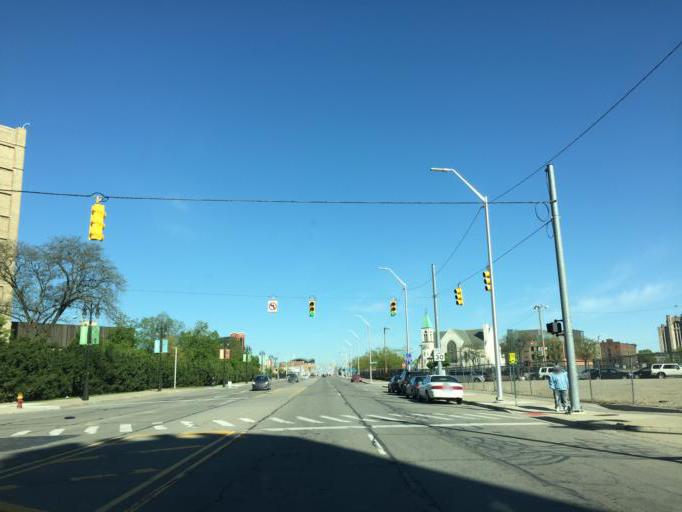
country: US
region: Michigan
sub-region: Wayne County
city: Detroit
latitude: 42.3351
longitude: -83.0555
